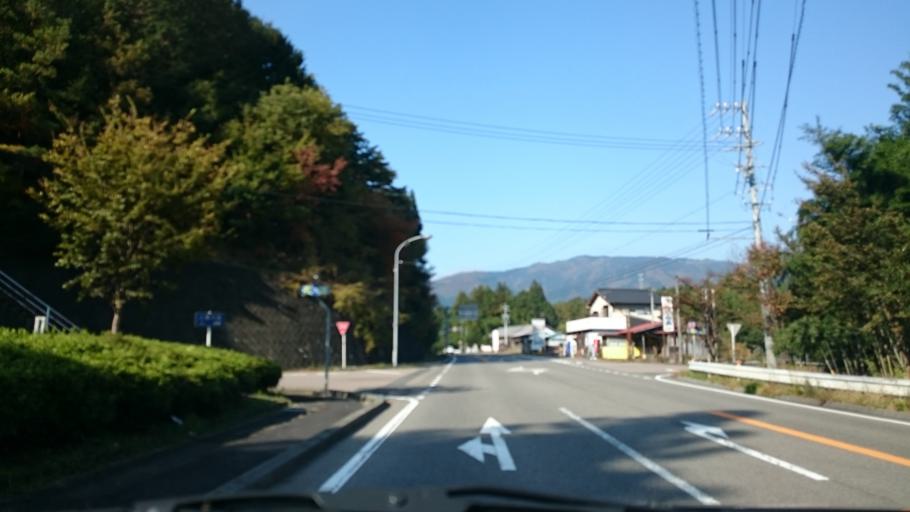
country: JP
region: Gifu
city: Nakatsugawa
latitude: 35.7479
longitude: 137.3297
